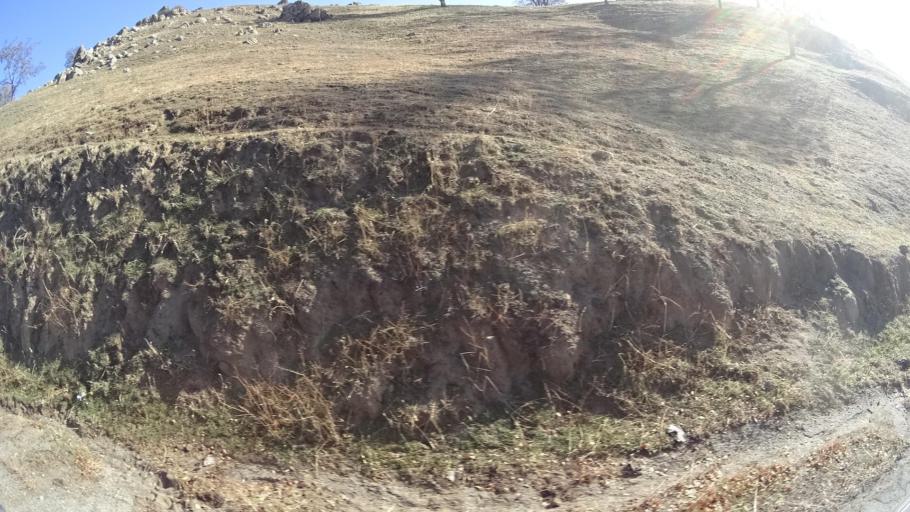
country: US
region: California
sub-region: Kern County
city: Alta Sierra
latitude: 35.7306
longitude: -118.8133
